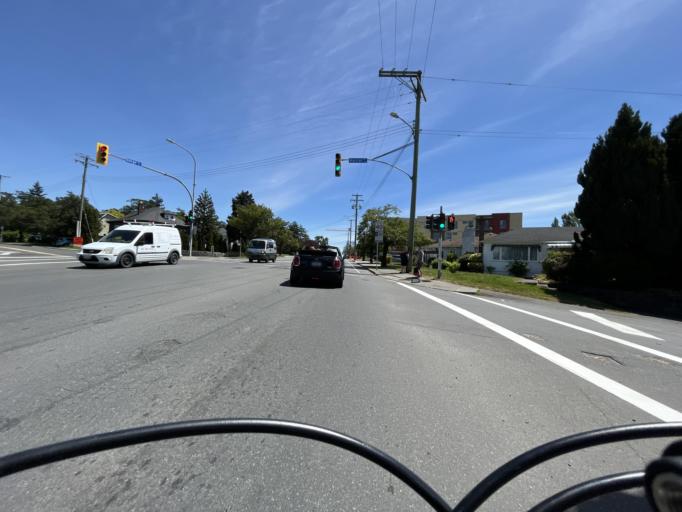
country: CA
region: British Columbia
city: Victoria
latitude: 48.4439
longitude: -123.3907
